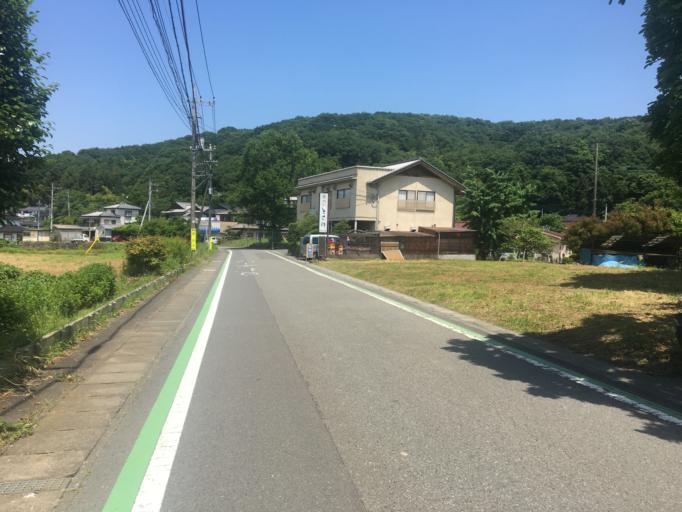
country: JP
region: Saitama
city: Ogawa
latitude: 36.0043
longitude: 139.2876
